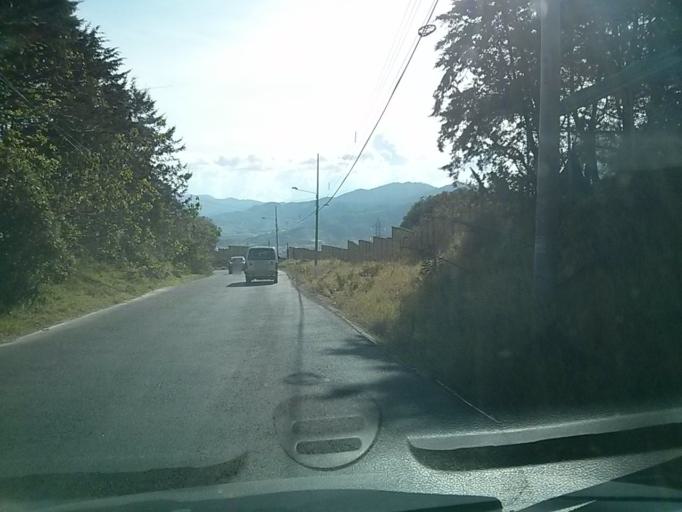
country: CR
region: Cartago
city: Cartago
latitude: 9.8895
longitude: -83.9193
